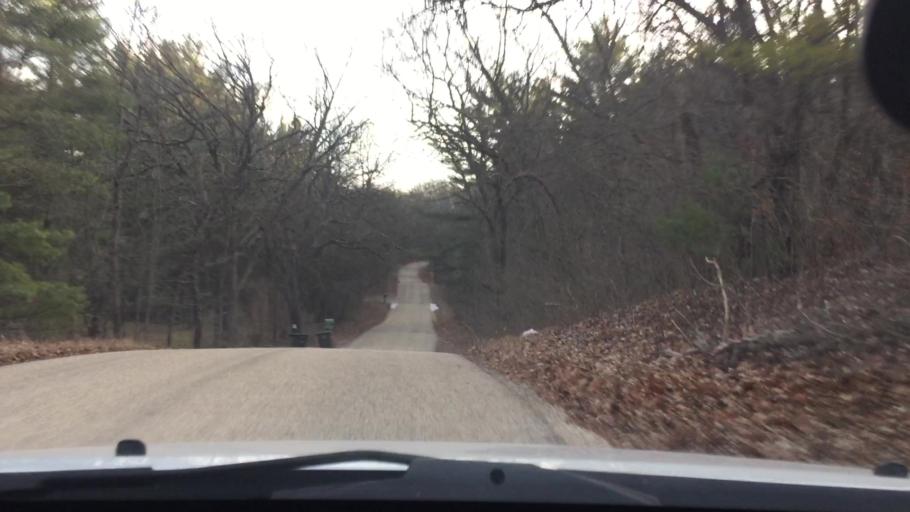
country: US
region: Wisconsin
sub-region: Waukesha County
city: North Prairie
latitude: 42.9397
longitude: -88.4348
